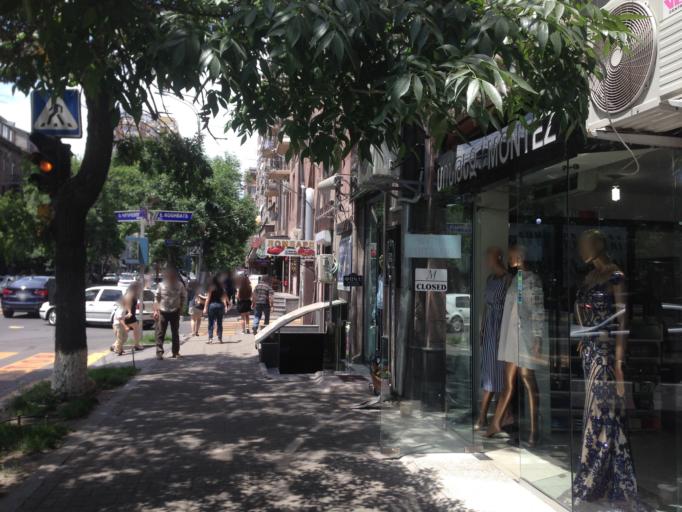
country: AM
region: Yerevan
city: Yerevan
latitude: 40.1799
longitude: 44.5095
